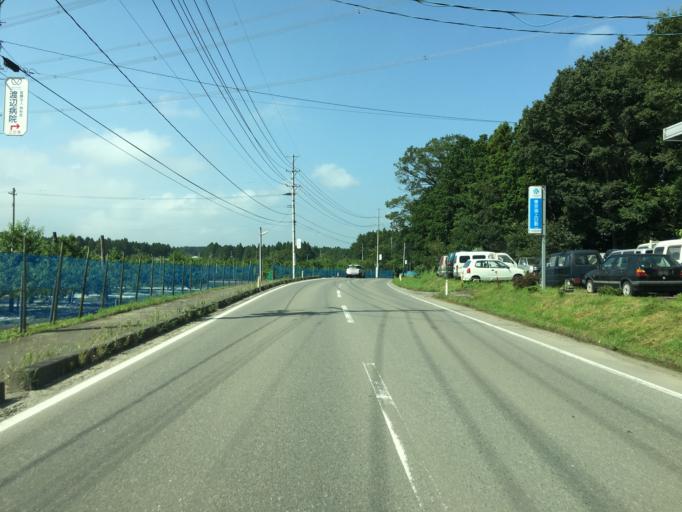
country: JP
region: Miyagi
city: Marumori
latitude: 37.8529
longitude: 140.8956
